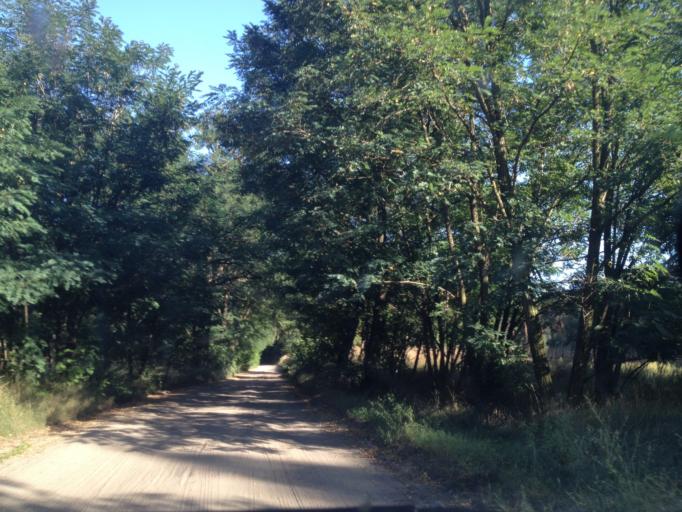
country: PL
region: Greater Poland Voivodeship
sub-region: Powiat sredzki
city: Zaniemysl
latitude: 52.1082
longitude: 17.1250
